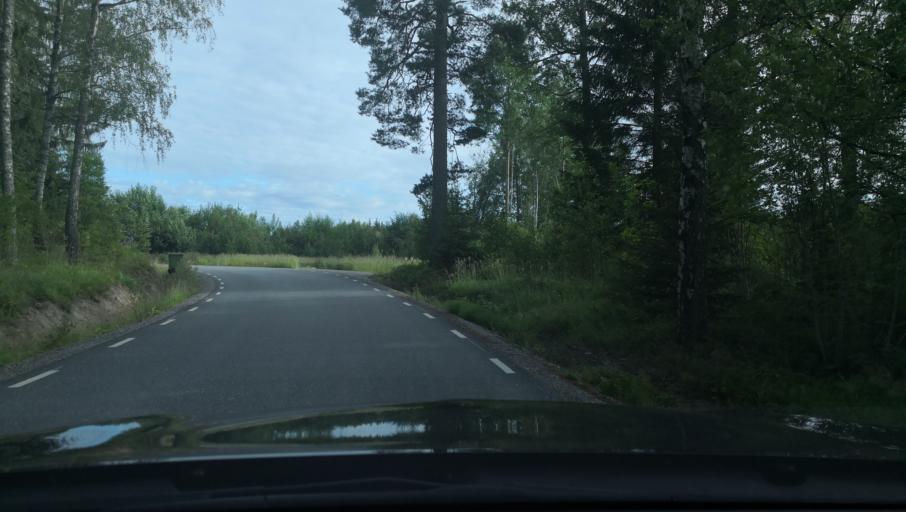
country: SE
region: Vaestmanland
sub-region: Surahammars Kommun
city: Surahammar
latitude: 59.6594
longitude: 16.1771
